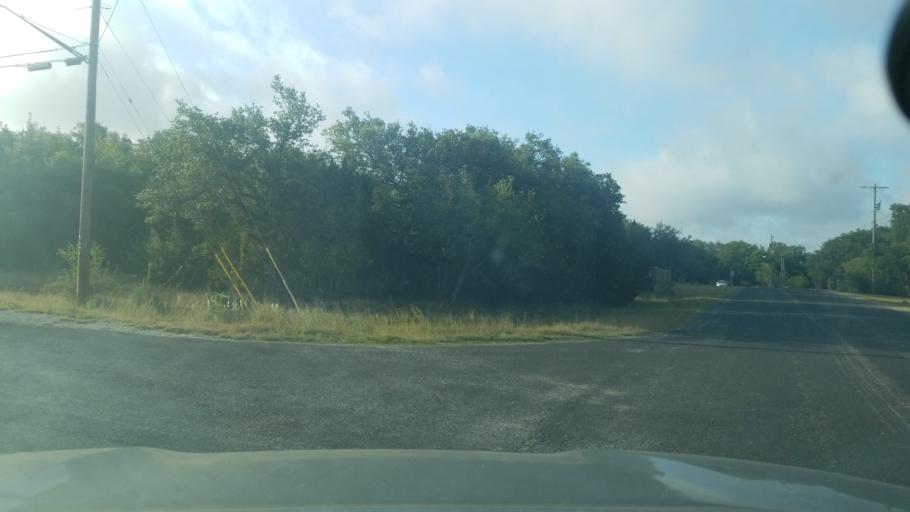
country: US
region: Texas
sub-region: Bexar County
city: Timberwood Park
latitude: 29.7006
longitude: -98.5054
